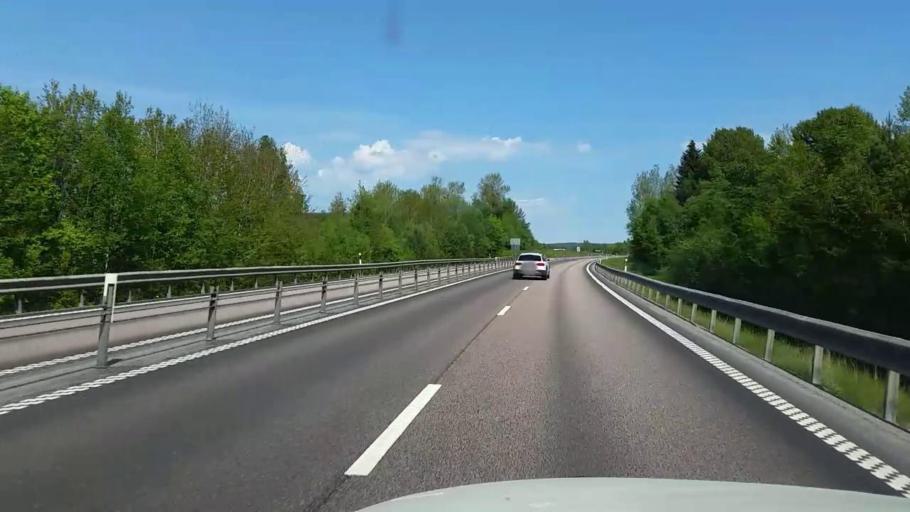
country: SE
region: Gaevleborg
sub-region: Hudiksvalls Kommun
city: Hudiksvall
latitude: 61.7512
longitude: 17.0805
